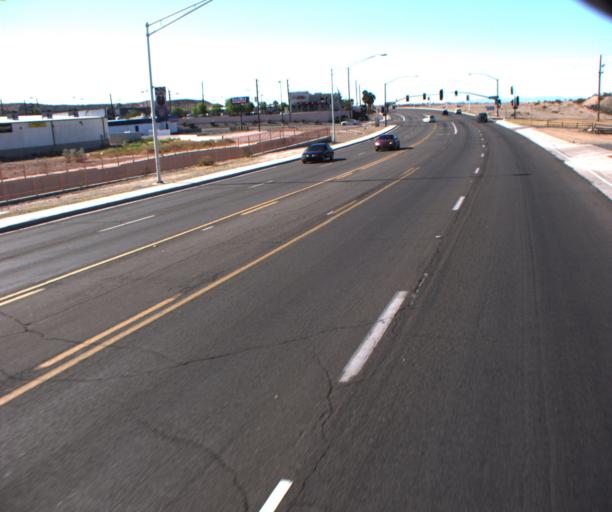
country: US
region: Arizona
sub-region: Mohave County
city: Bullhead City
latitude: 35.0855
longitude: -114.5979
